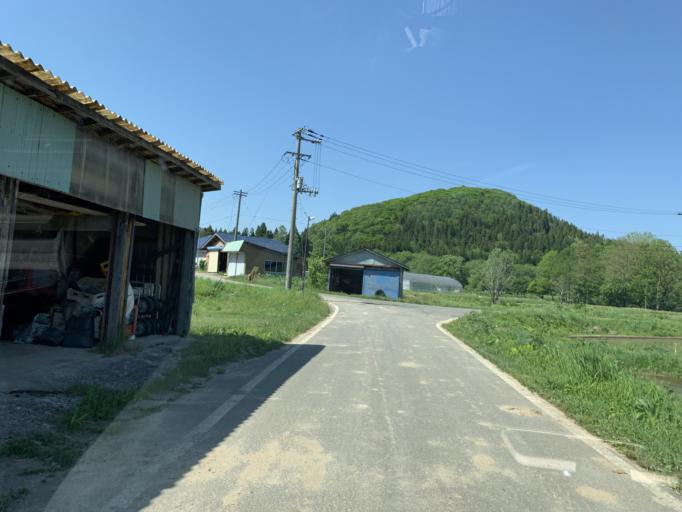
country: JP
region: Iwate
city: Shizukuishi
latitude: 39.5662
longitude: 140.8318
